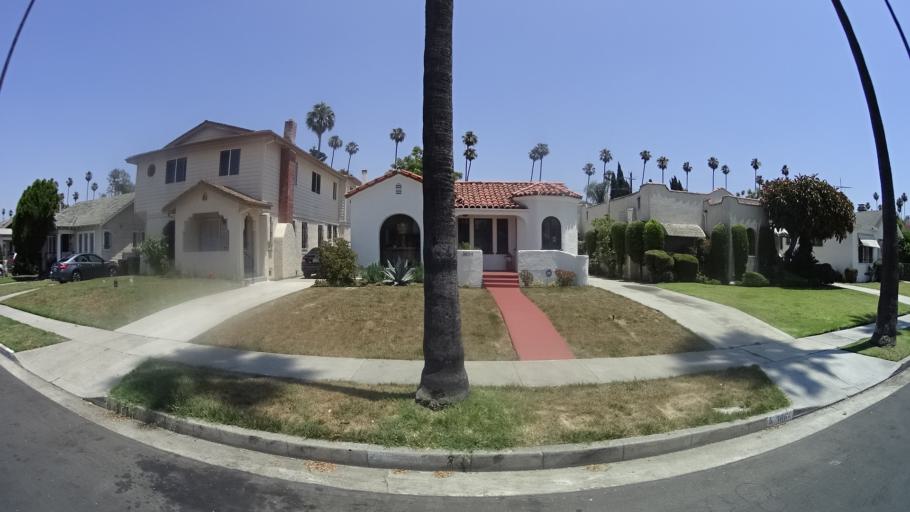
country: US
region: California
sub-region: Los Angeles County
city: View Park-Windsor Hills
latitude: 34.0159
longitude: -118.3204
